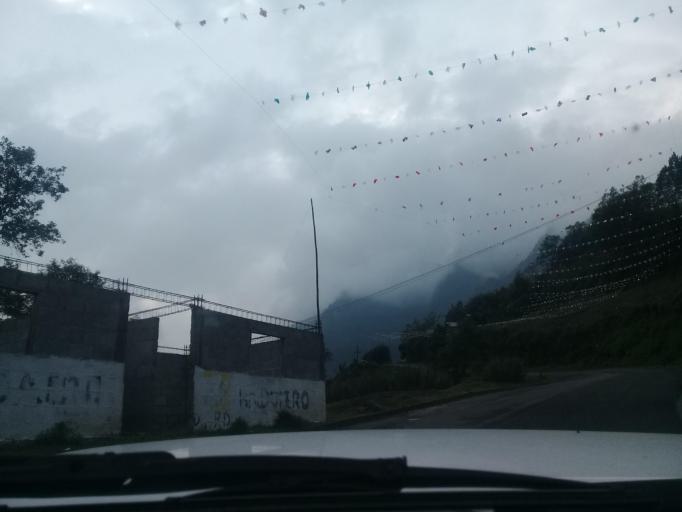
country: MX
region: Veracruz
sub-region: Mariano Escobedo
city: San Isidro el Berro
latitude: 18.9545
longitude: -97.1969
